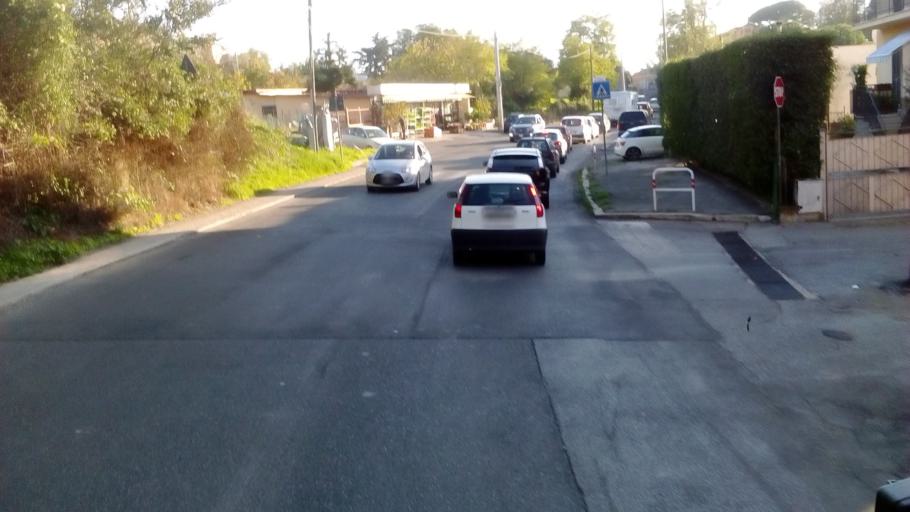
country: IT
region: Latium
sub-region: Citta metropolitana di Roma Capitale
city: Pavona
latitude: 41.7333
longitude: 12.6168
